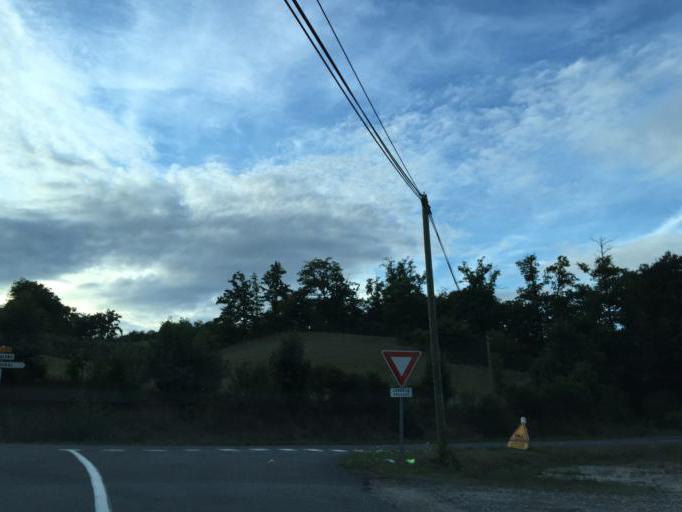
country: FR
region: Midi-Pyrenees
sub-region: Departement de l'Aveyron
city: Pont-de-Salars
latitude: 44.2986
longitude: 2.7256
